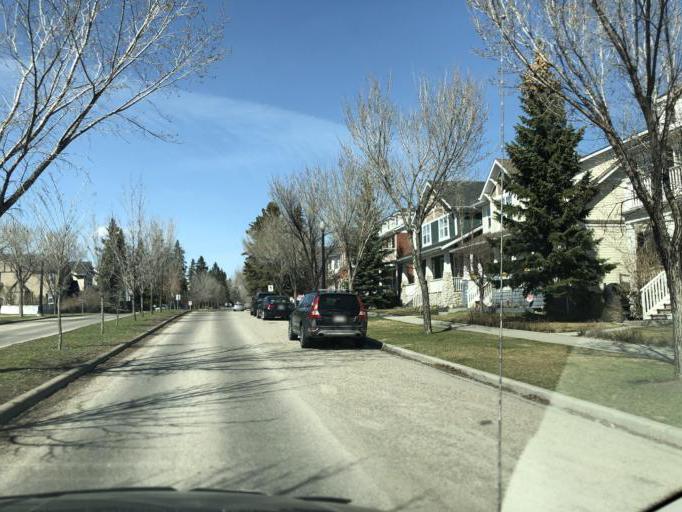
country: CA
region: Alberta
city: Calgary
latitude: 51.0176
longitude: -114.1138
